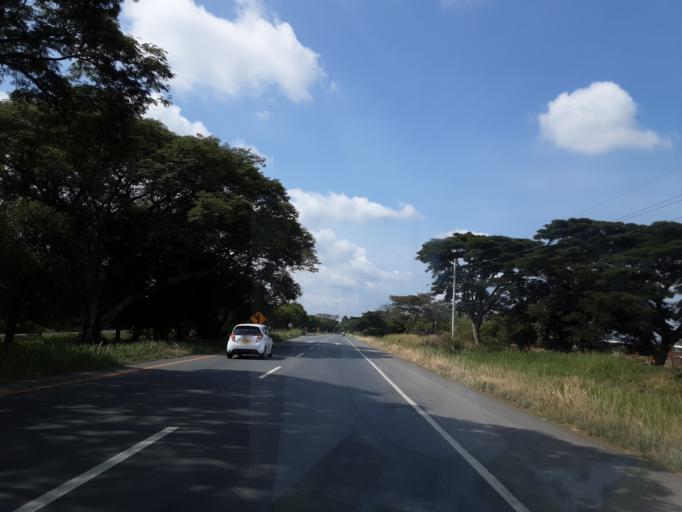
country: CO
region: Valle del Cauca
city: Guacari
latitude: 3.7560
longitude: -76.3261
